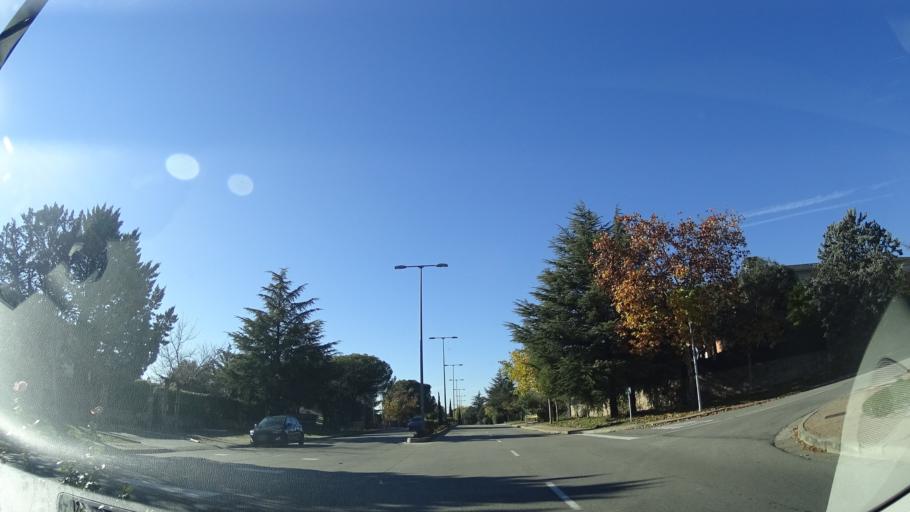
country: ES
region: Madrid
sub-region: Provincia de Madrid
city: Las Matas
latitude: 40.5339
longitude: -3.9032
